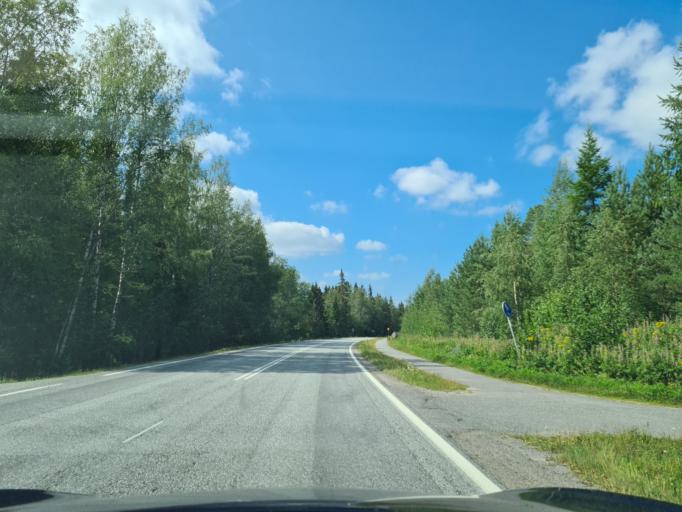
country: FI
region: Ostrobothnia
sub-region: Vaasa
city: Vaasa
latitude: 63.1952
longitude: 21.5489
